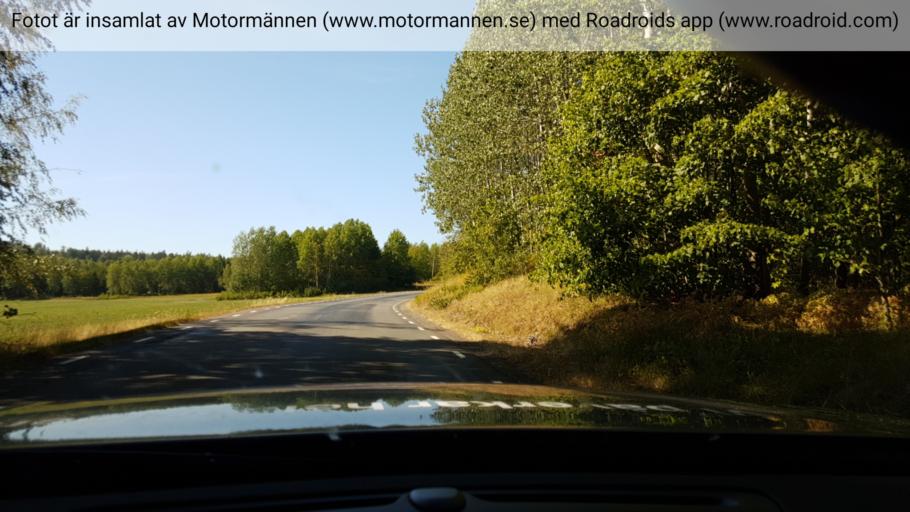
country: SE
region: Vaestra Goetaland
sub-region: Karlsborgs Kommun
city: Molltorp
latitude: 58.6614
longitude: 14.3889
